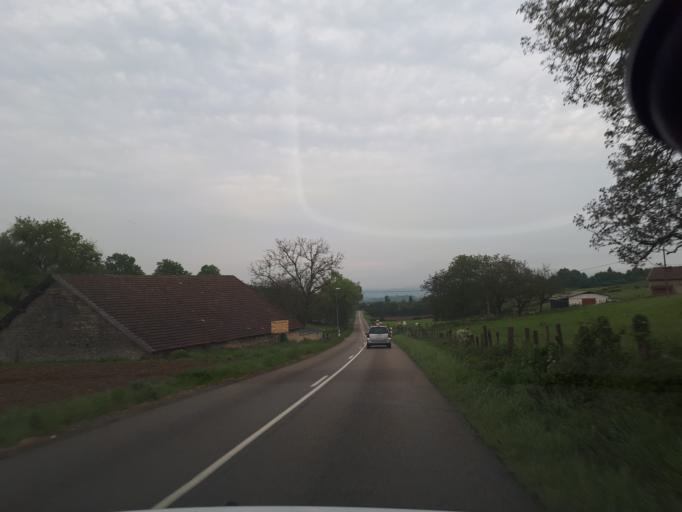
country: FR
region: Rhone-Alpes
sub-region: Departement de l'Isere
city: L'Isle-d'Abeau
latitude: 45.6486
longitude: 5.2250
